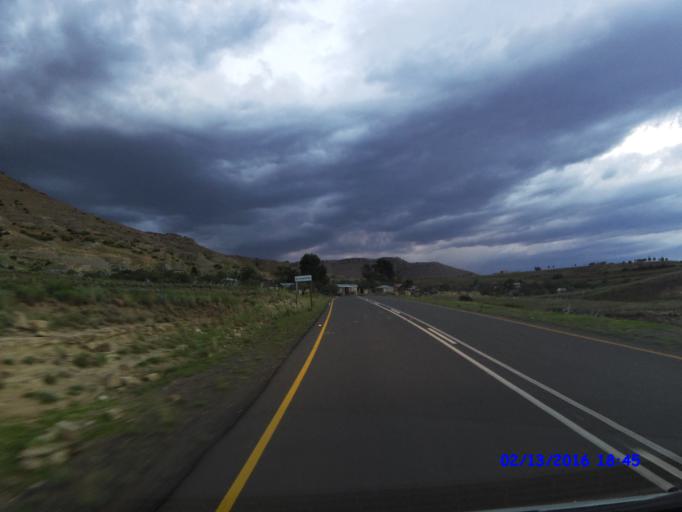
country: LS
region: Qacha's Nek
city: Qacha's Nek
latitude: -30.0566
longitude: 28.3008
